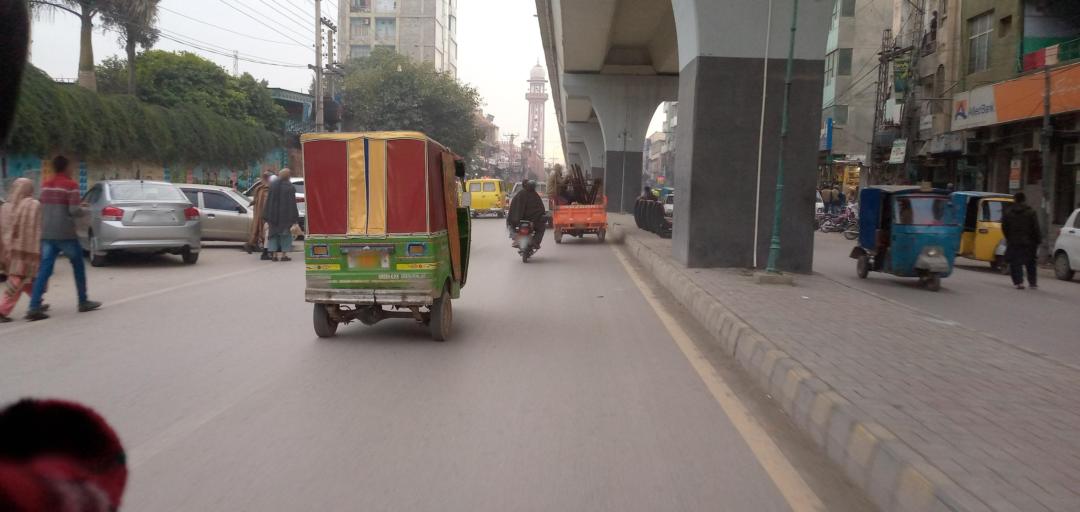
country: PK
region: Khyber Pakhtunkhwa
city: Peshawar
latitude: 33.9973
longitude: 71.5418
